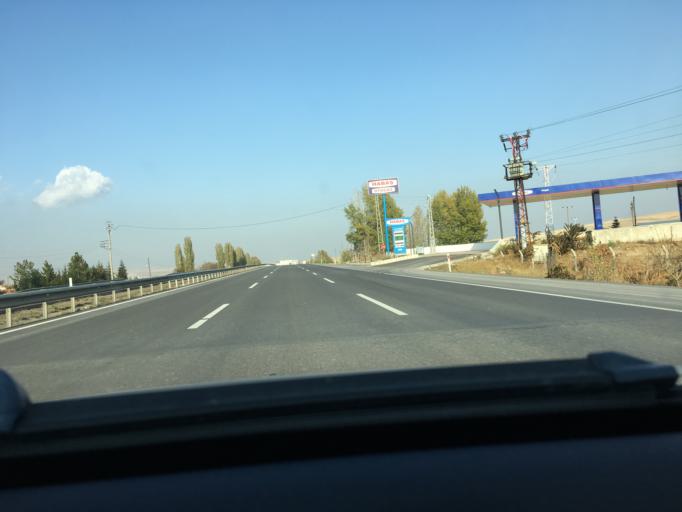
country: TR
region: Ankara
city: Polatli
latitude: 39.6710
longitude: 32.2311
